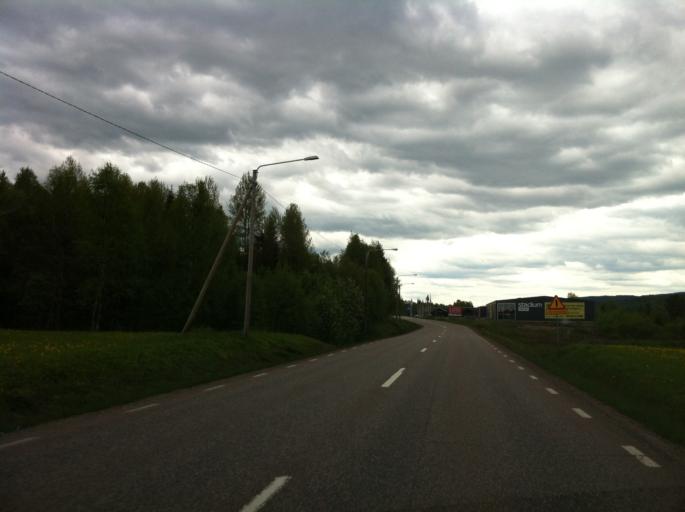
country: SE
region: Dalarna
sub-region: Malung-Saelens kommun
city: Malung
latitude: 61.1391
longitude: 13.2791
